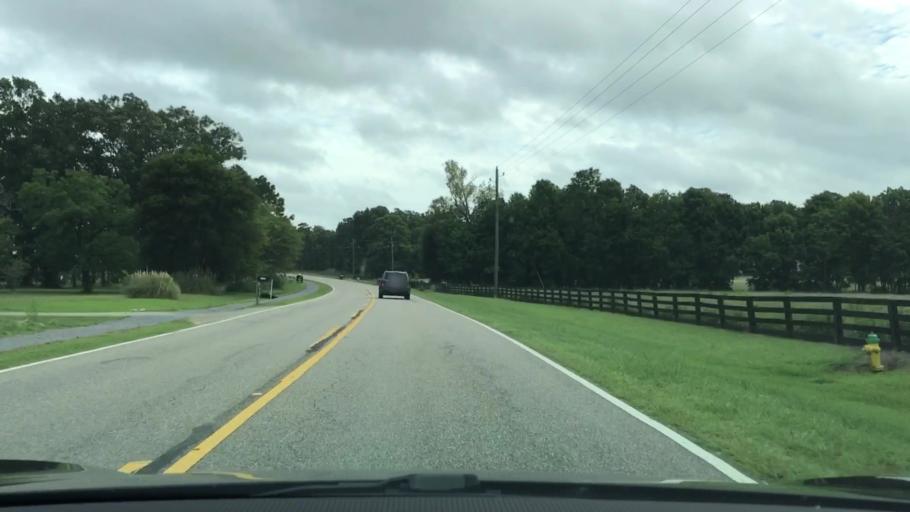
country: US
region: Alabama
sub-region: Montgomery County
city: Pike Road
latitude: 32.3082
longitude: -86.0478
